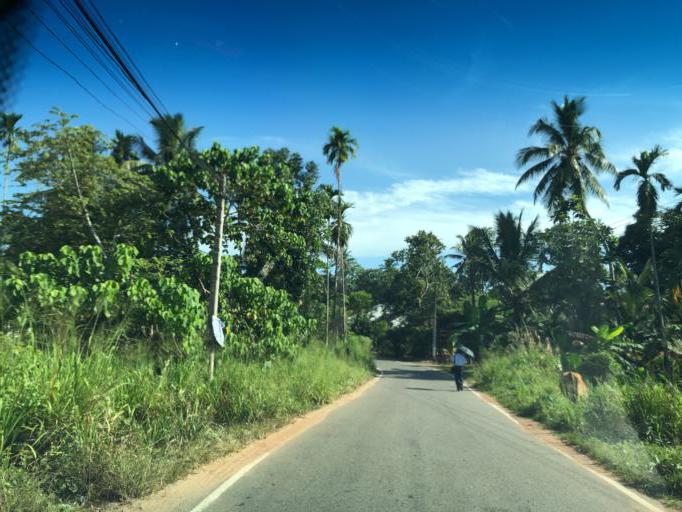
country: LK
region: Western
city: Homagama
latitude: 6.7899
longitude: 79.9787
